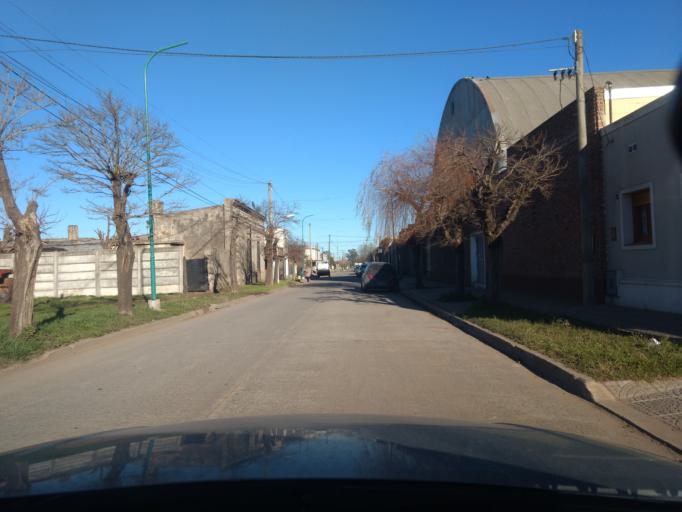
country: AR
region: Buenos Aires
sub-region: Partido de Navarro
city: Navarro
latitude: -35.0011
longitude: -59.2787
